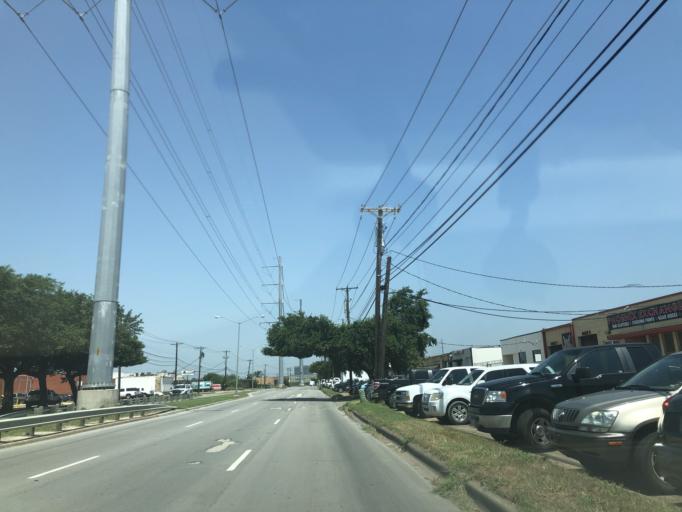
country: US
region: Texas
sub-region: Dallas County
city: Dallas
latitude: 32.7978
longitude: -96.8383
